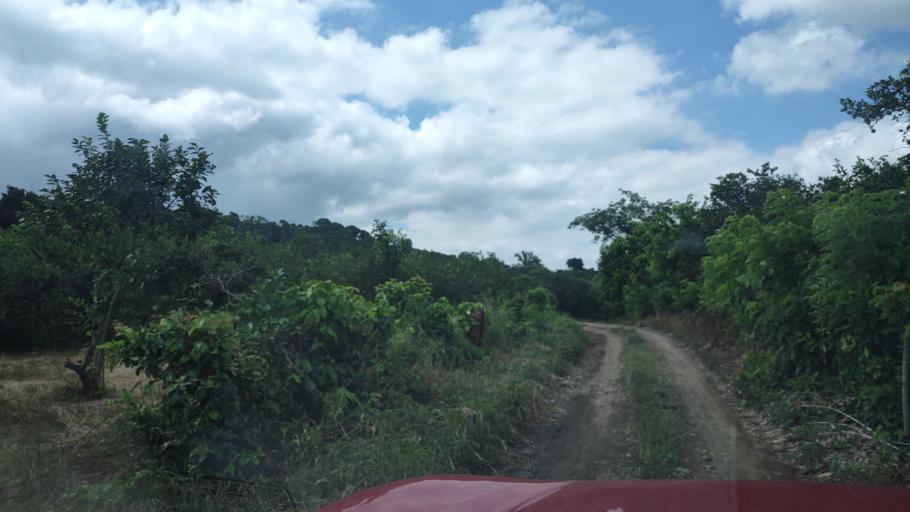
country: MX
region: Puebla
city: San Jose Acateno
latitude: 20.2244
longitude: -97.1575
